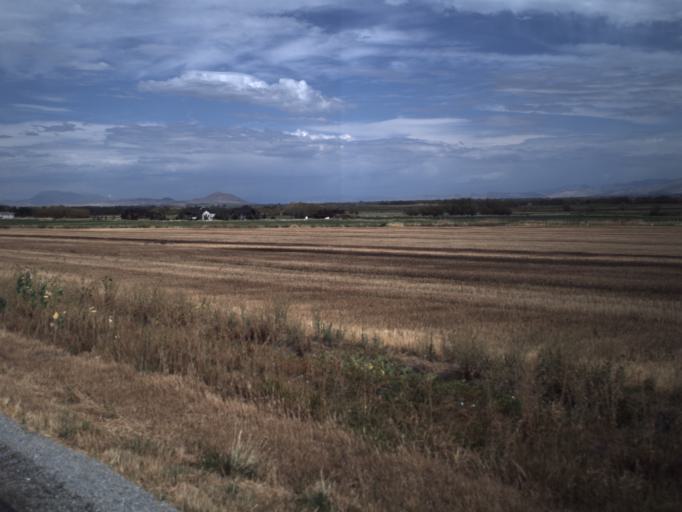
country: US
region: Utah
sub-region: Cache County
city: Mendon
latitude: 41.6757
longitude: -111.9577
